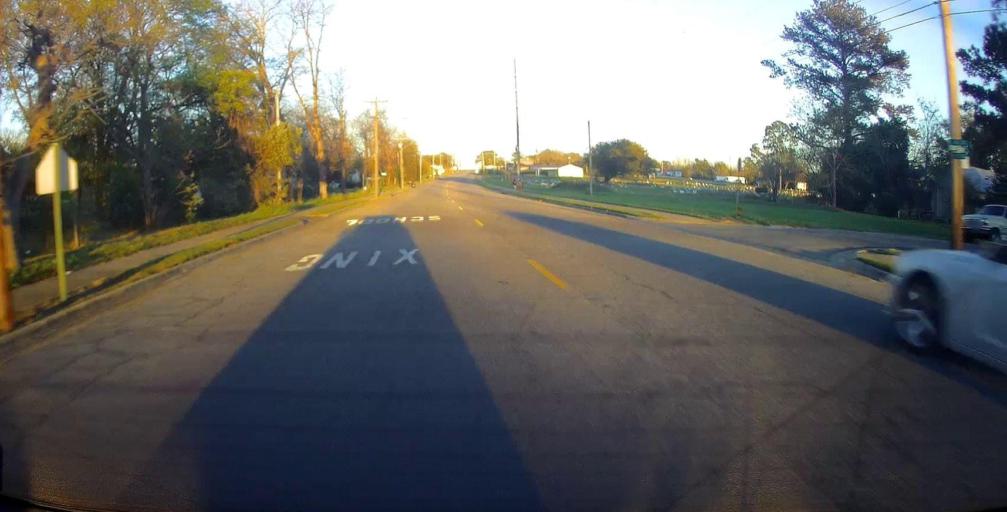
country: US
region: Georgia
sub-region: Crisp County
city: Cordele
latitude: 31.9553
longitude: -83.7933
